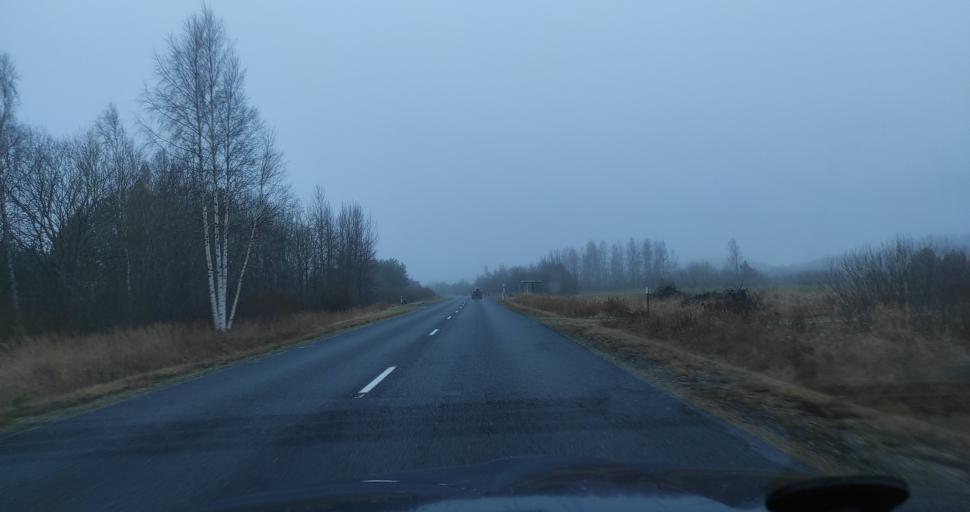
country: LV
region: Alsunga
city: Alsunga
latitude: 57.1159
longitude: 21.4237
